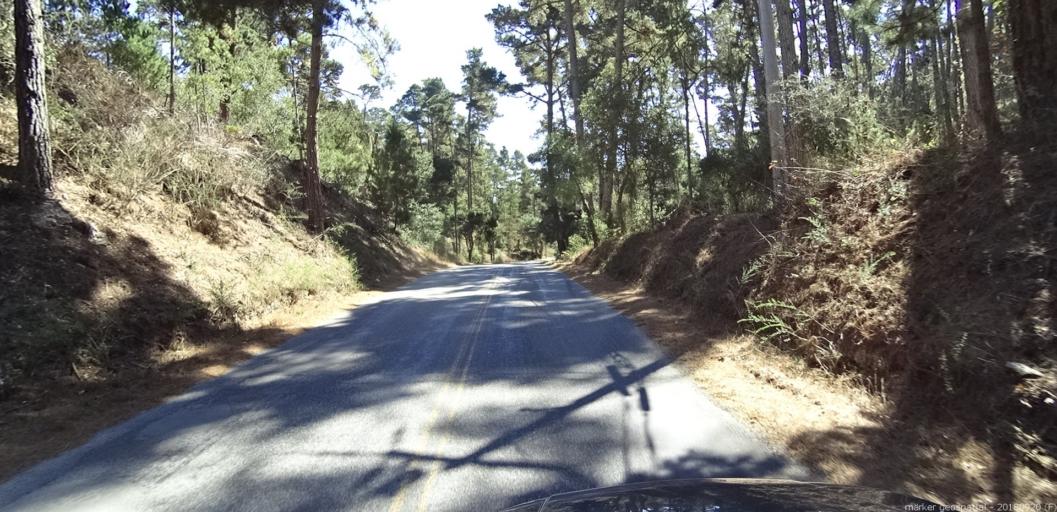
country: US
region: California
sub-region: Monterey County
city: Carmel-by-the-Sea
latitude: 36.5721
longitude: -121.9059
